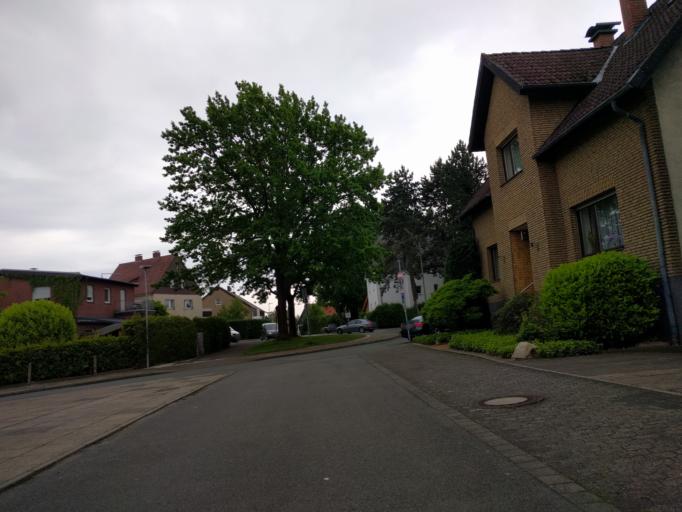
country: DE
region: North Rhine-Westphalia
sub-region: Regierungsbezirk Detmold
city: Bielefeld
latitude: 52.0490
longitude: 8.5505
